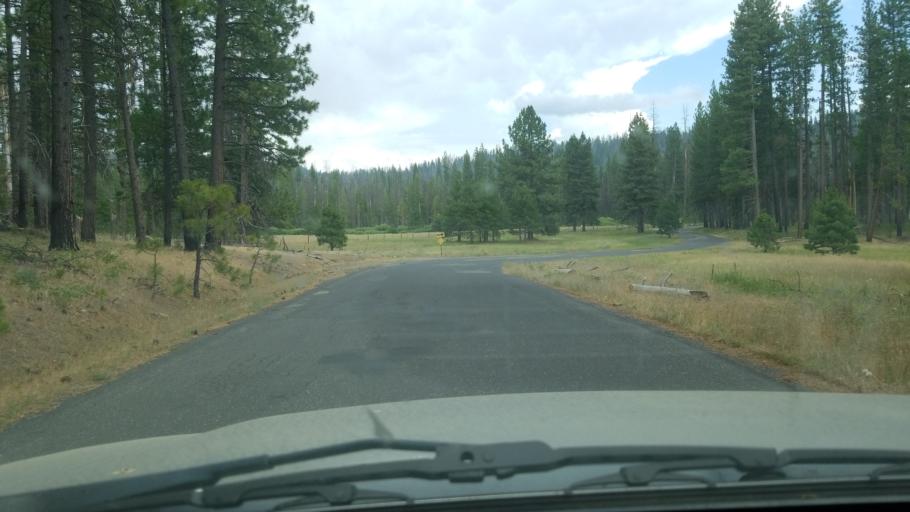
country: US
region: California
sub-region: Mariposa County
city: Yosemite Valley
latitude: 37.8372
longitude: -119.8484
